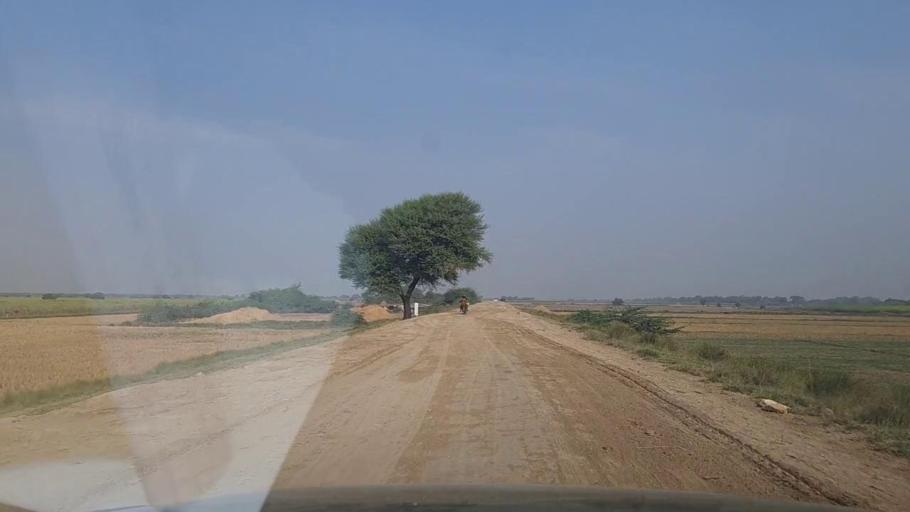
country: PK
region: Sindh
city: Bulri
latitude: 25.0101
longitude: 68.2860
